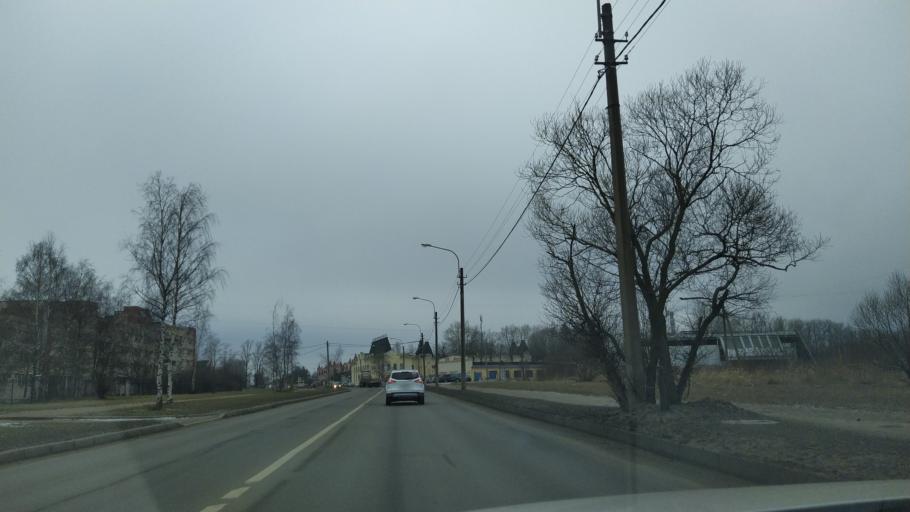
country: RU
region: St.-Petersburg
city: Pushkin
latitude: 59.7337
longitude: 30.3873
